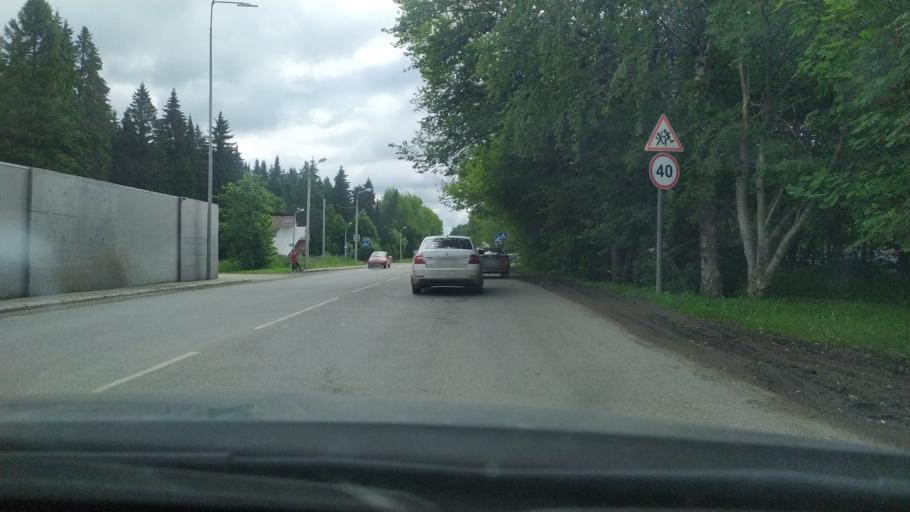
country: RU
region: Perm
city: Froly
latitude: 57.9758
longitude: 56.3202
